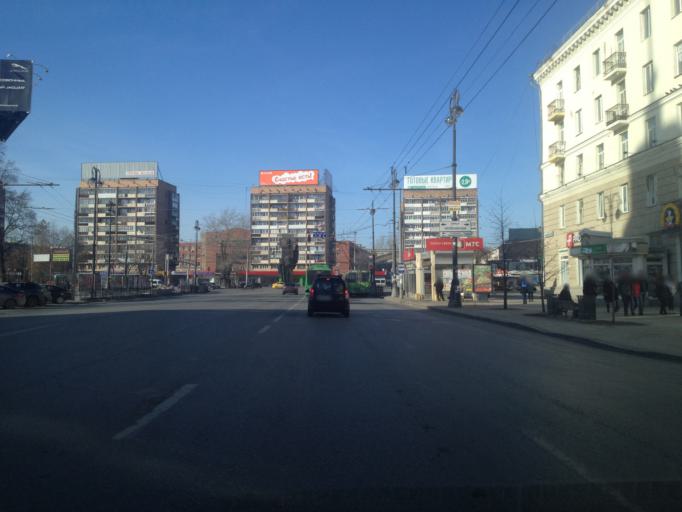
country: RU
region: Sverdlovsk
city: Yekaterinburg
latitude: 56.8552
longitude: 60.6044
